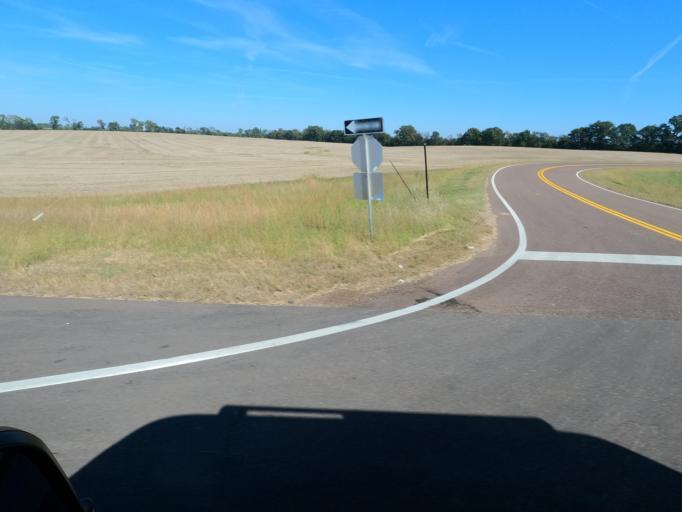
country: US
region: Tennessee
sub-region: Dyer County
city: Dyersburg
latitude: 35.9542
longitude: -89.3178
